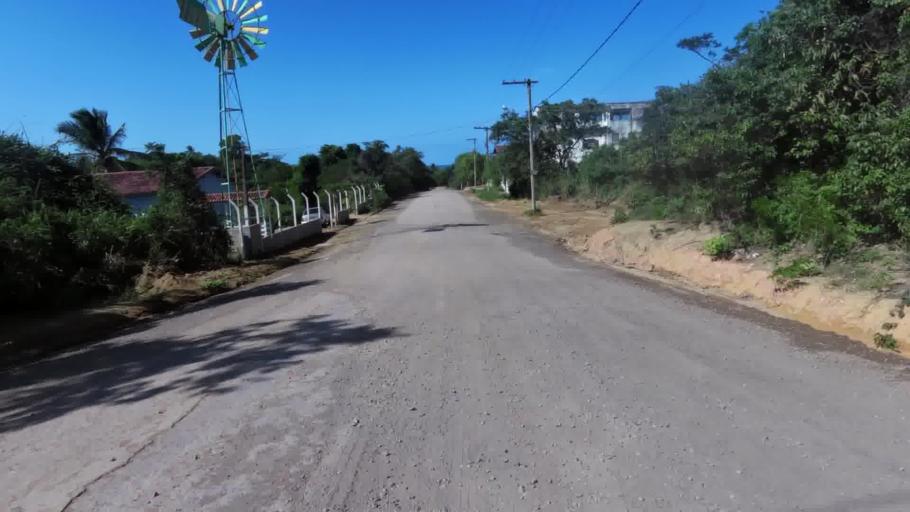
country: BR
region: Espirito Santo
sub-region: Piuma
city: Piuma
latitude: -20.8241
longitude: -40.6199
